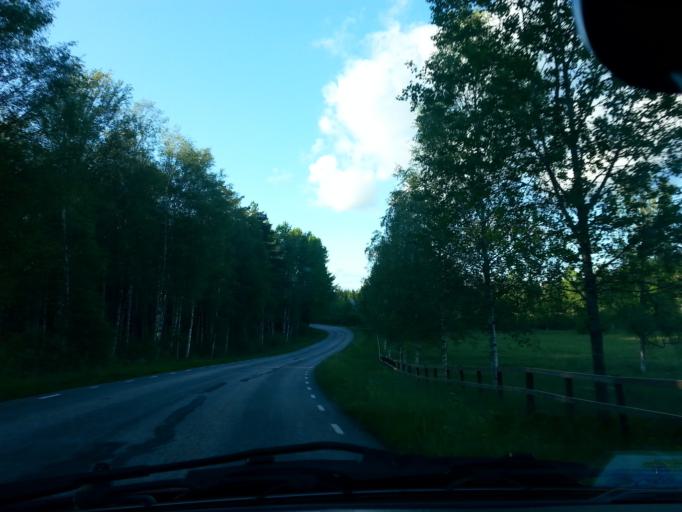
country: SE
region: Joenkoeping
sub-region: Gislaveds Kommun
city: Reftele
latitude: 57.2321
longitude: 13.6419
